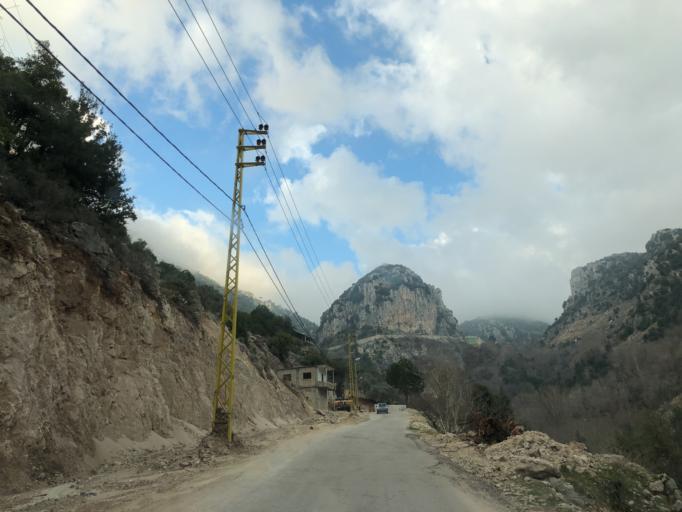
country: LB
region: Liban-Nord
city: Amioun
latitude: 34.1977
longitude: 35.8861
